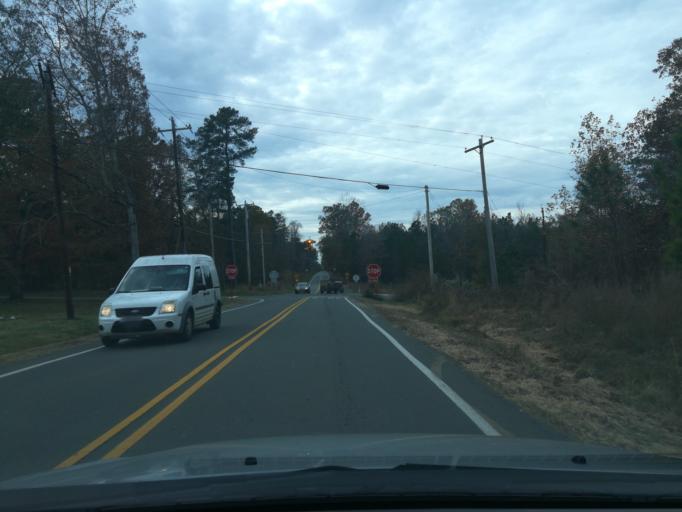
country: US
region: North Carolina
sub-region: Orange County
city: Hillsborough
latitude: 36.0314
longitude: -79.0213
